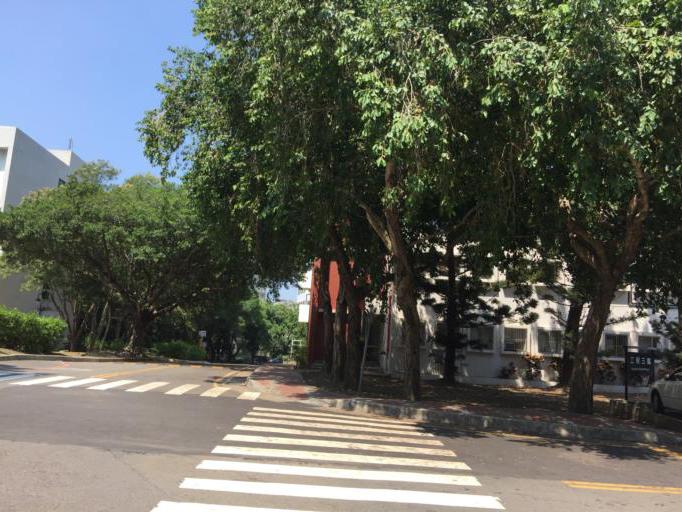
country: TW
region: Taiwan
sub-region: Hsinchu
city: Hsinchu
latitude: 24.7961
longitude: 120.9924
